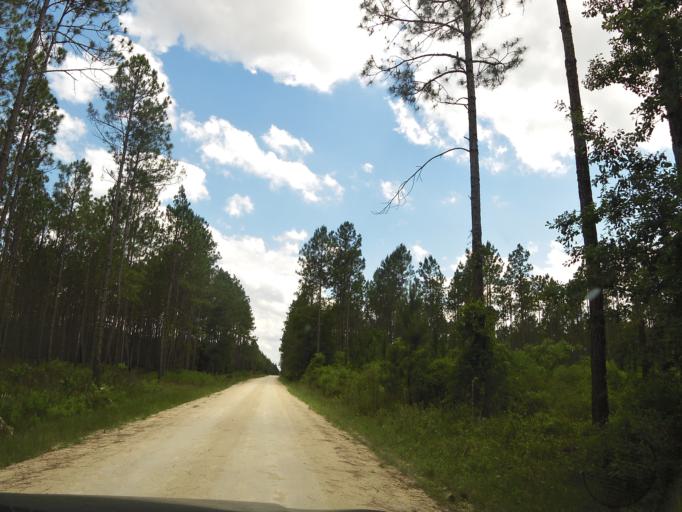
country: US
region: Florida
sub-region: Clay County
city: Asbury Lake
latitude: 29.8746
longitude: -81.8530
